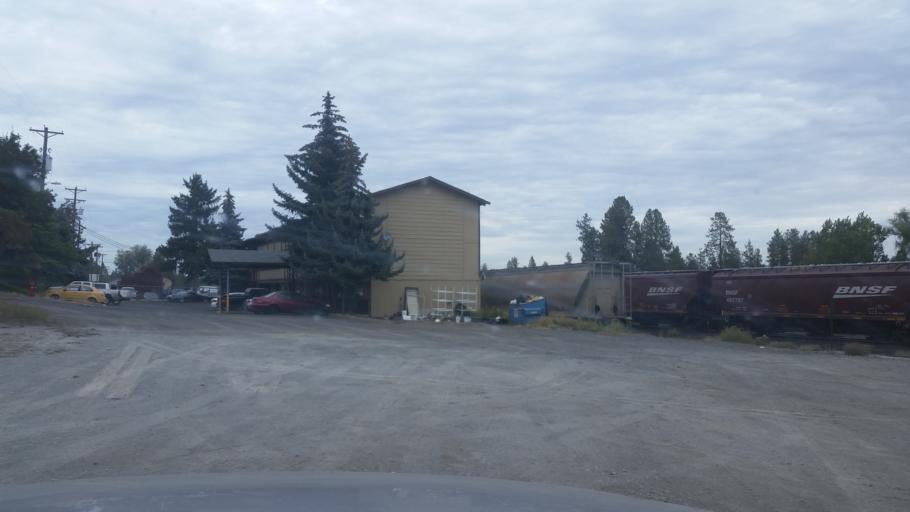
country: US
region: Washington
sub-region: Spokane County
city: Cheney
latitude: 47.4889
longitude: -117.5726
